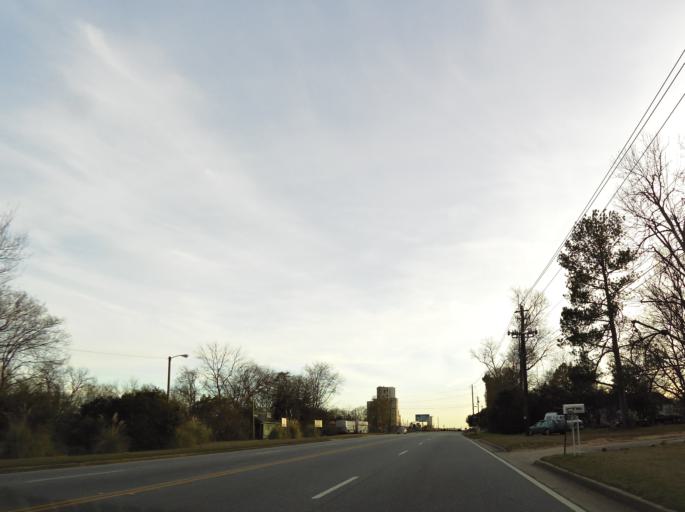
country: US
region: Georgia
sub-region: Bibb County
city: Macon
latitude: 32.7864
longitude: -83.6528
